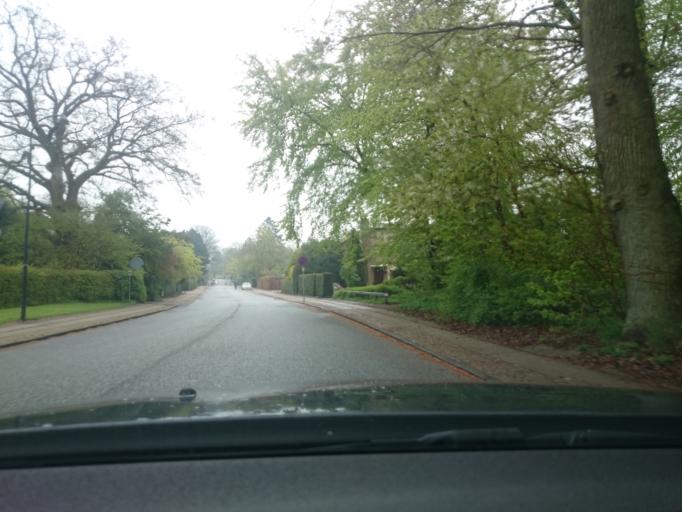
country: DK
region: Capital Region
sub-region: Gentofte Kommune
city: Charlottenlund
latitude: 55.7684
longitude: 12.5650
